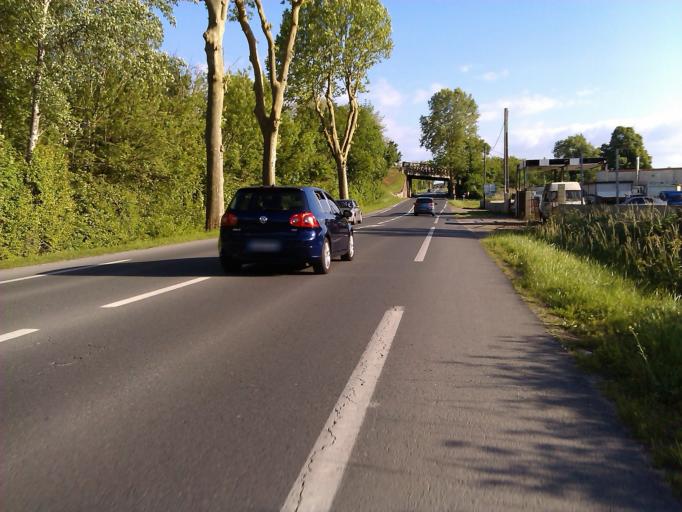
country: FR
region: Aquitaine
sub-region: Departement de la Gironde
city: Cubzac-les-Ponts
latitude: 44.9803
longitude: -0.4514
